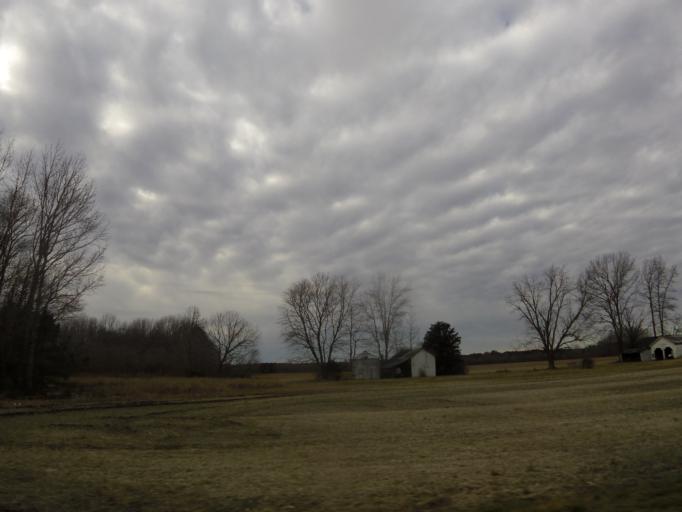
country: US
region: North Carolina
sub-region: Hertford County
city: Murfreesboro
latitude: 36.4163
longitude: -77.1466
